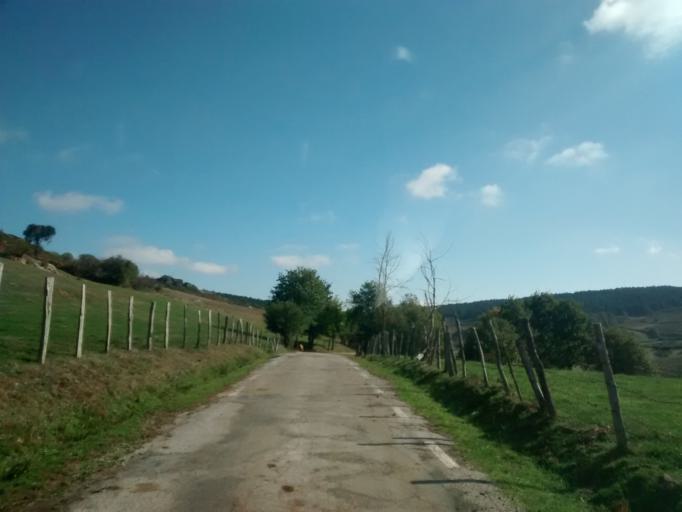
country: ES
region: Castille and Leon
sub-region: Provincia de Burgos
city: Arija
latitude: 42.9274
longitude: -3.9991
